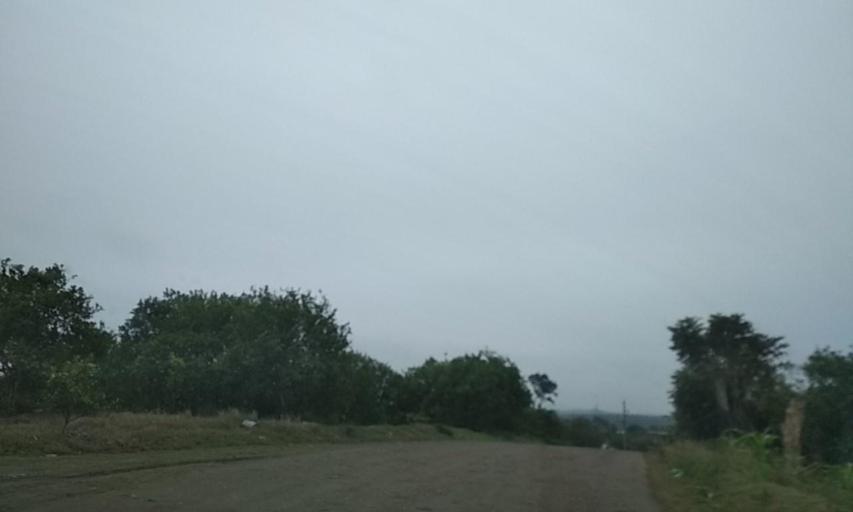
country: MX
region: Veracruz
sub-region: Papantla
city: El Chote
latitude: 20.3328
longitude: -97.3913
